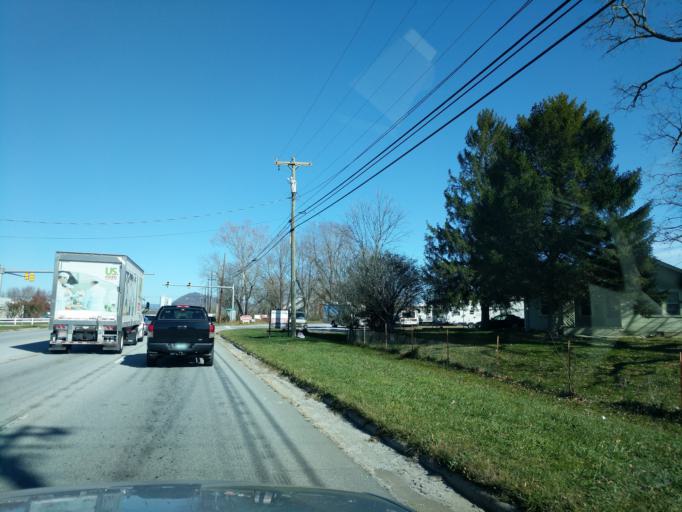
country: US
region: North Carolina
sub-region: Henderson County
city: Fletcher
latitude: 35.4126
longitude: -82.5100
